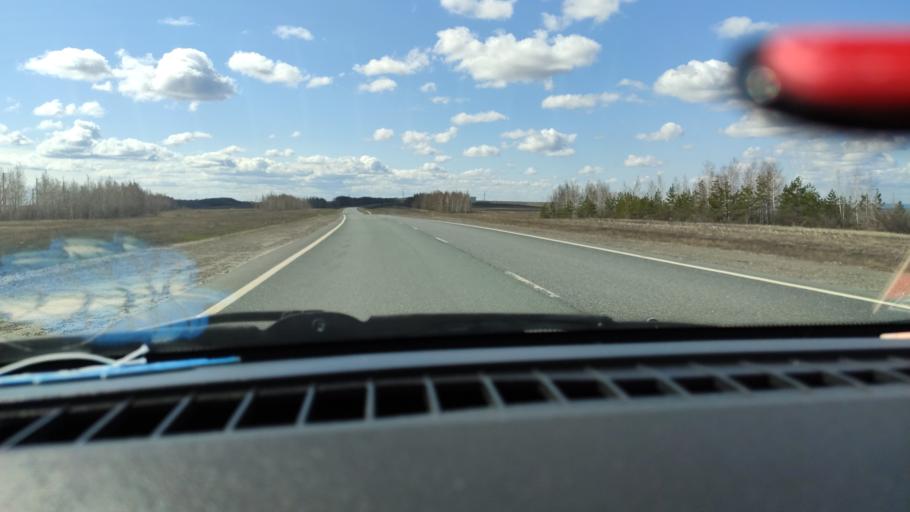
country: RU
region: Saratov
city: Dukhovnitskoye
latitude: 52.8507
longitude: 48.2567
